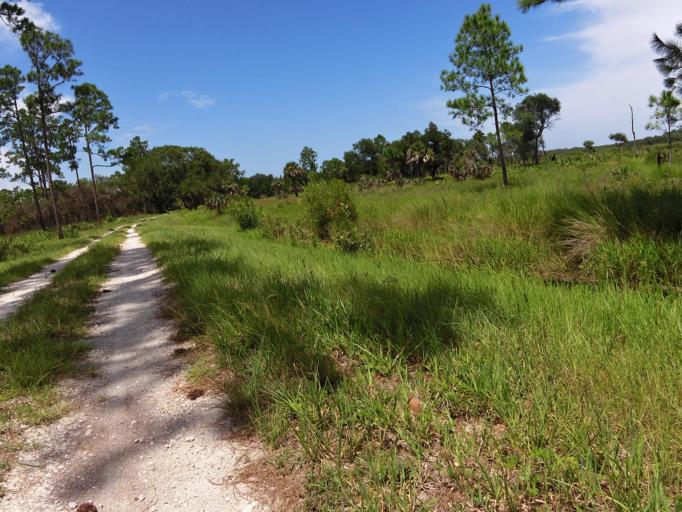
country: US
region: Florida
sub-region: Saint Johns County
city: Villano Beach
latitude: 30.0447
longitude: -81.3440
